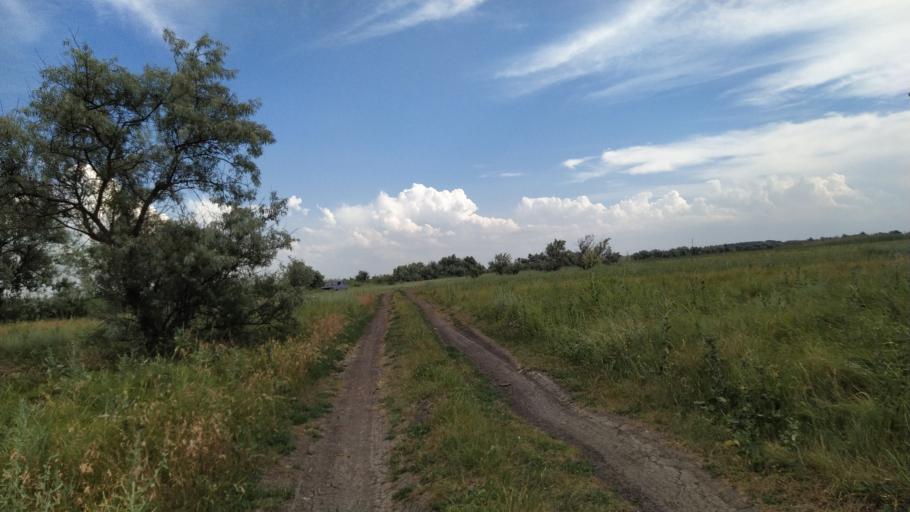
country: RU
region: Rostov
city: Kuleshovka
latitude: 47.1295
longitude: 39.6295
